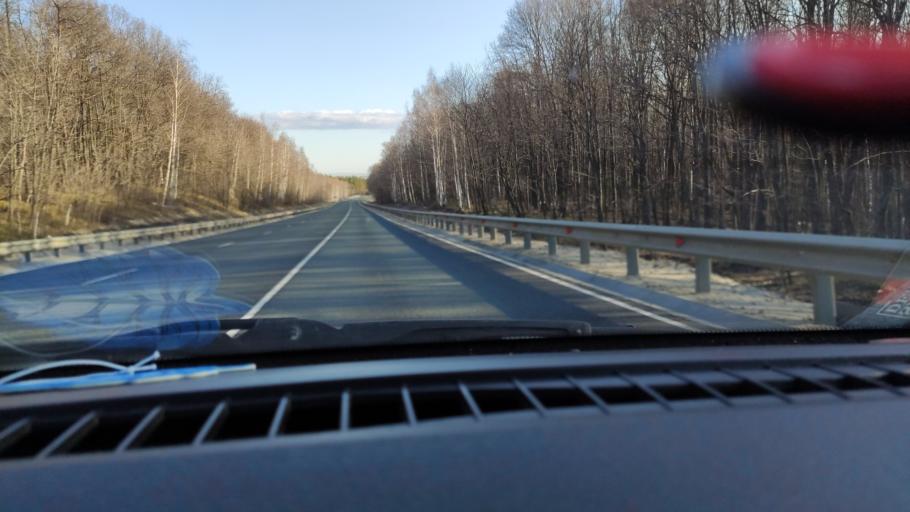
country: RU
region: Saratov
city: Khvalynsk
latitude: 52.5093
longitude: 48.0159
